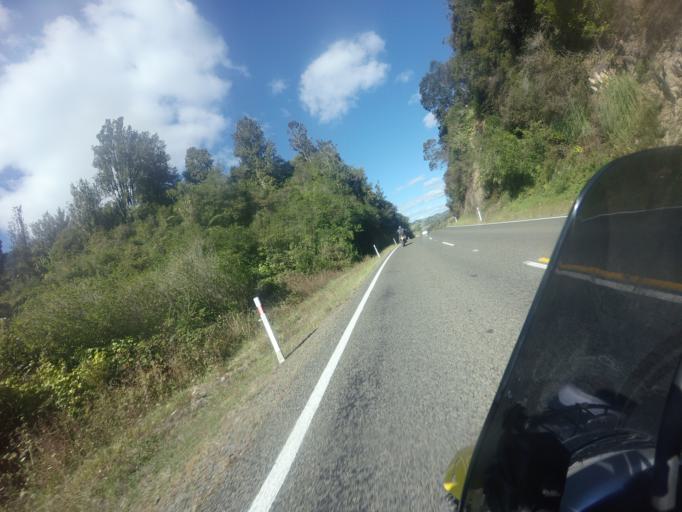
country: NZ
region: Bay of Plenty
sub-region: Opotiki District
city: Opotiki
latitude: -38.0577
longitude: 177.1255
